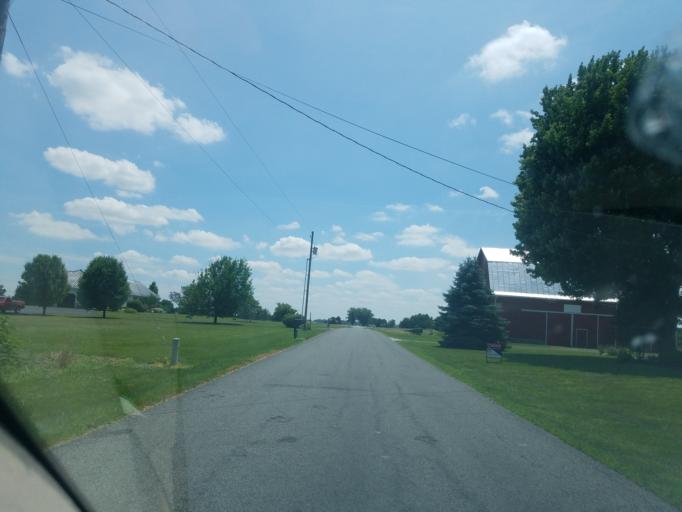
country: US
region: Ohio
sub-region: Wyandot County
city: Carey
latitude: 40.9687
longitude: -83.4768
